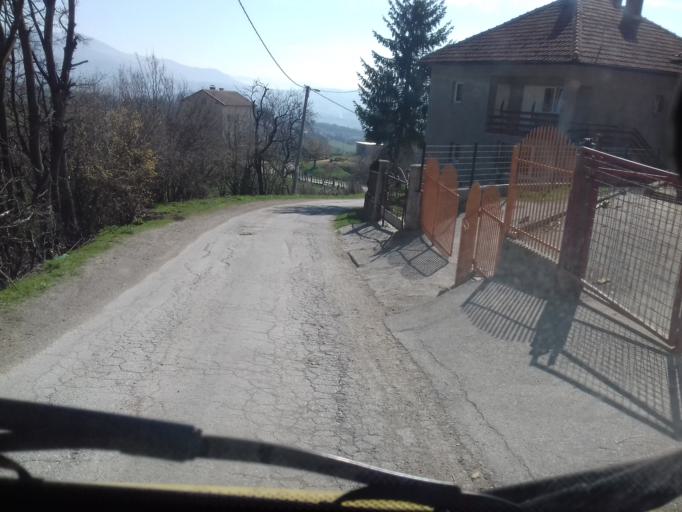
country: BA
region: Federation of Bosnia and Herzegovina
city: Travnik
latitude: 44.2429
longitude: 17.7201
